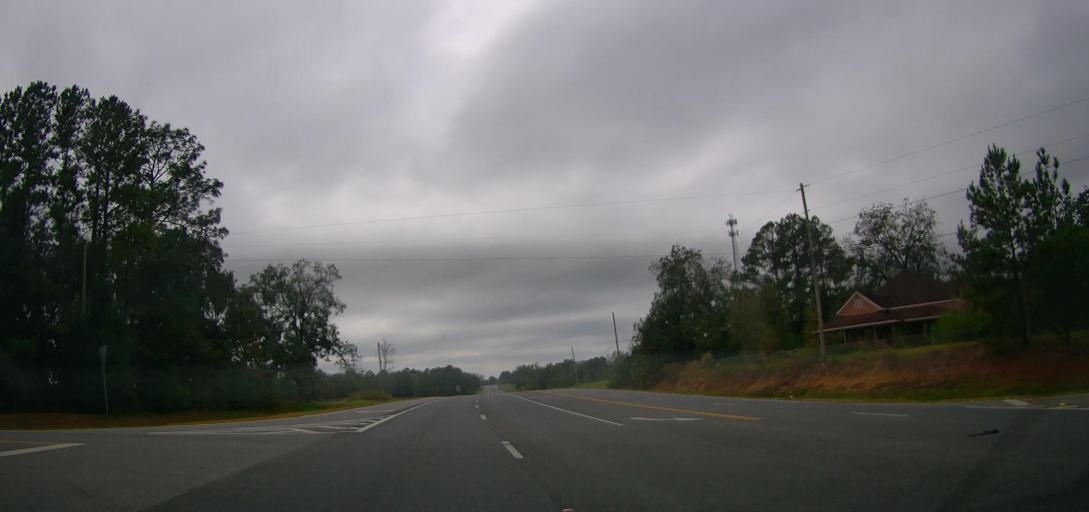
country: US
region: Georgia
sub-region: Thomas County
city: Thomasville
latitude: 30.9504
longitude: -83.8983
